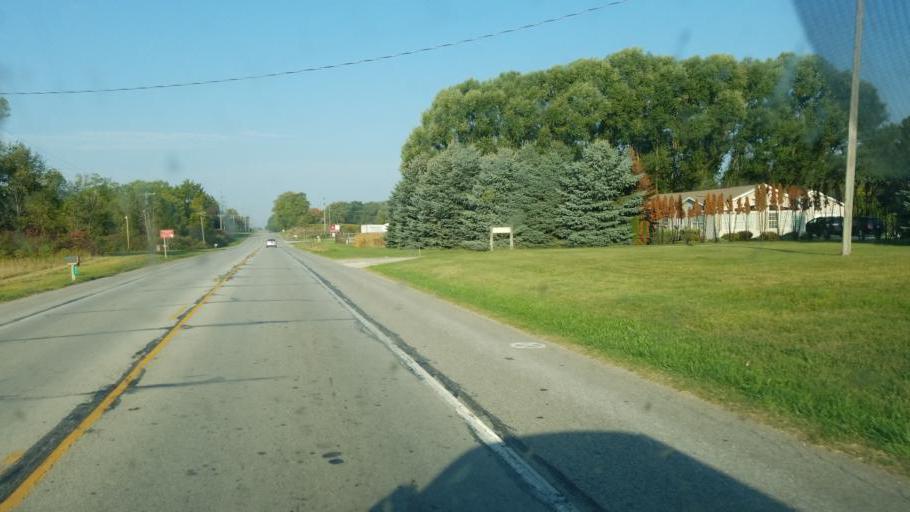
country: US
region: Indiana
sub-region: LaGrange County
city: Lagrange
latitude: 41.6413
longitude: -85.4407
